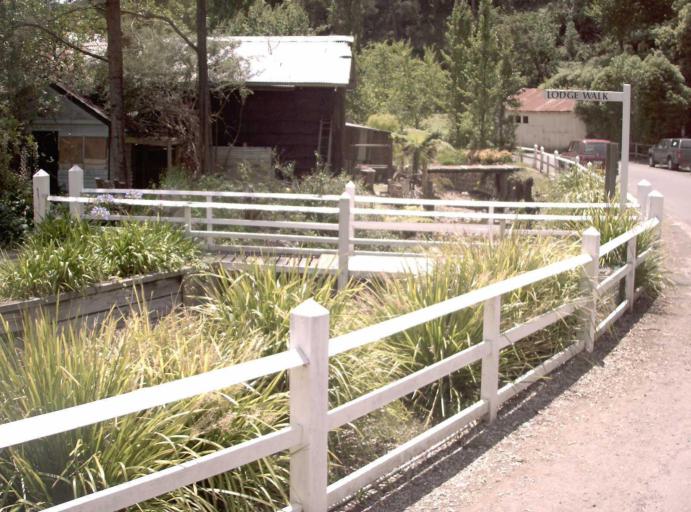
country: AU
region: Victoria
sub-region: Latrobe
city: Traralgon
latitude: -37.9417
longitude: 146.4519
